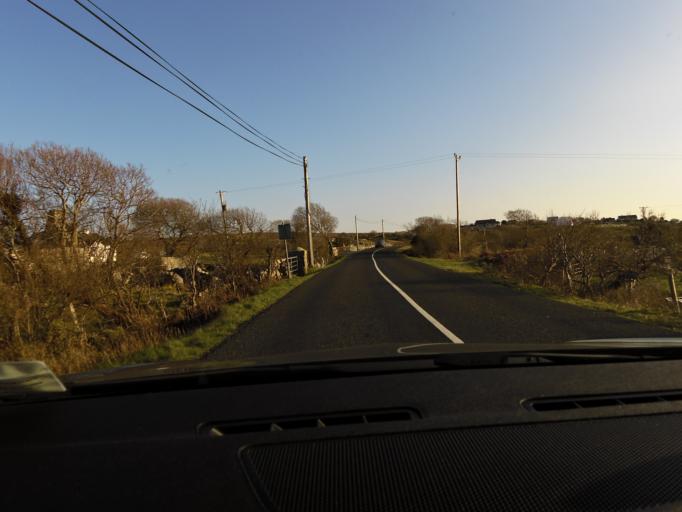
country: IE
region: Connaught
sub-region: County Galway
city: Oughterard
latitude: 53.3237
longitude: -9.5458
